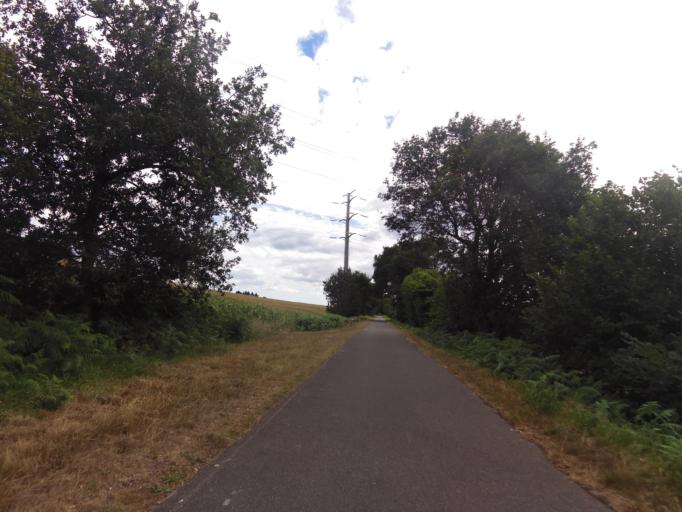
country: FR
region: Brittany
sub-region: Departement du Morbihan
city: Guillac
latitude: 47.9038
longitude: -2.4331
